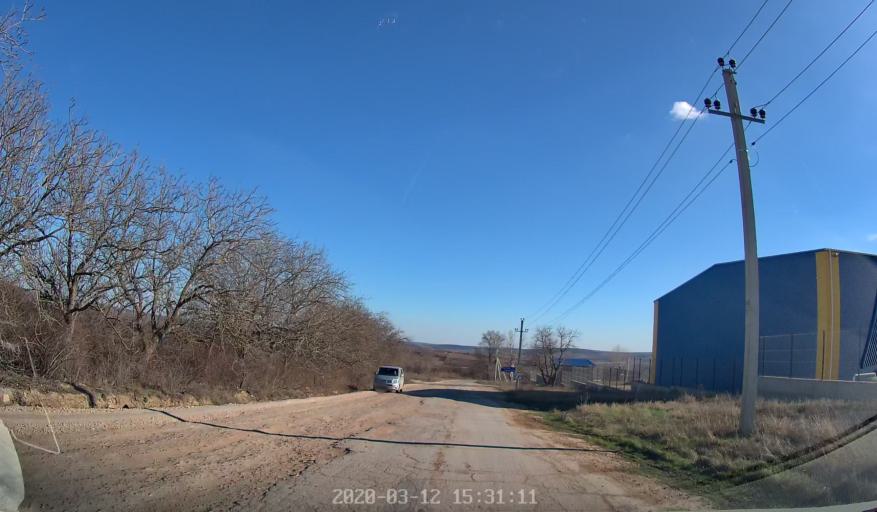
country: MD
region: Chisinau
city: Ciorescu
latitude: 47.1581
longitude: 28.9419
